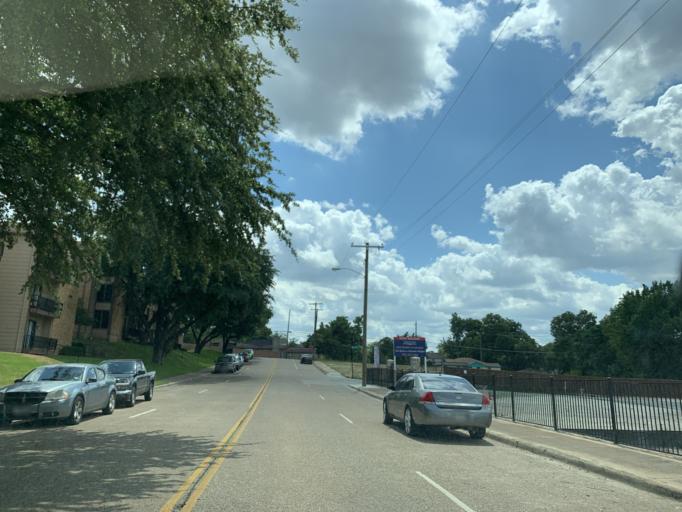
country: US
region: Texas
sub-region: Dallas County
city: Cockrell Hill
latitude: 32.7507
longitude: -96.8525
